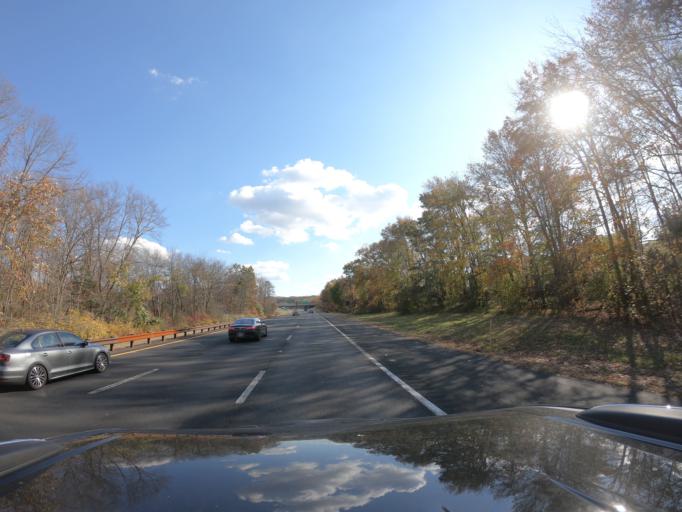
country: US
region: New Jersey
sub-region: Monmouth County
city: Strathmore
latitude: 40.4117
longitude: -74.2022
